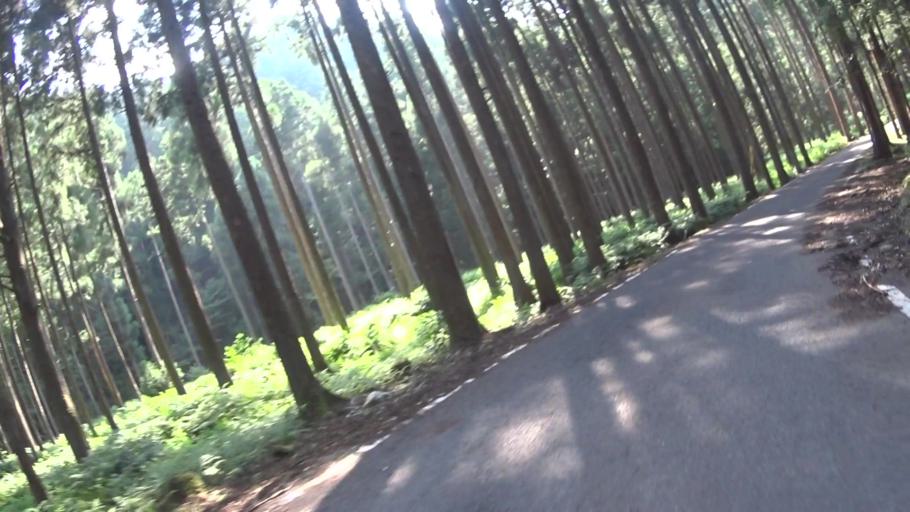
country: JP
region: Fukui
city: Obama
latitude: 35.2952
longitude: 135.6368
